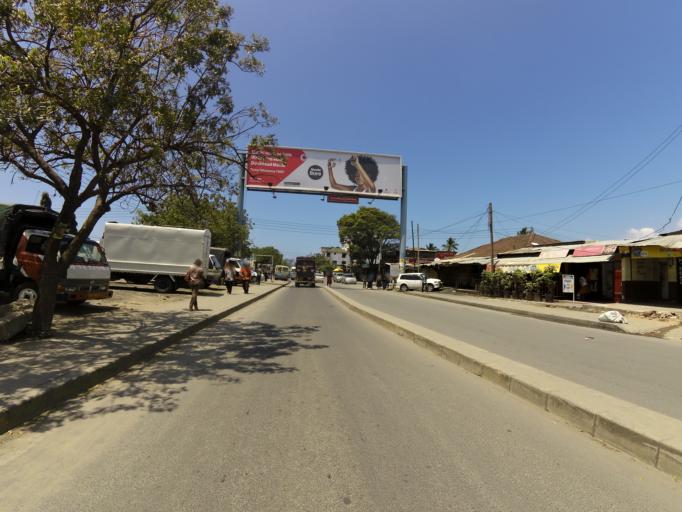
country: TZ
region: Dar es Salaam
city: Magomeni
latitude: -6.7901
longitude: 39.2639
